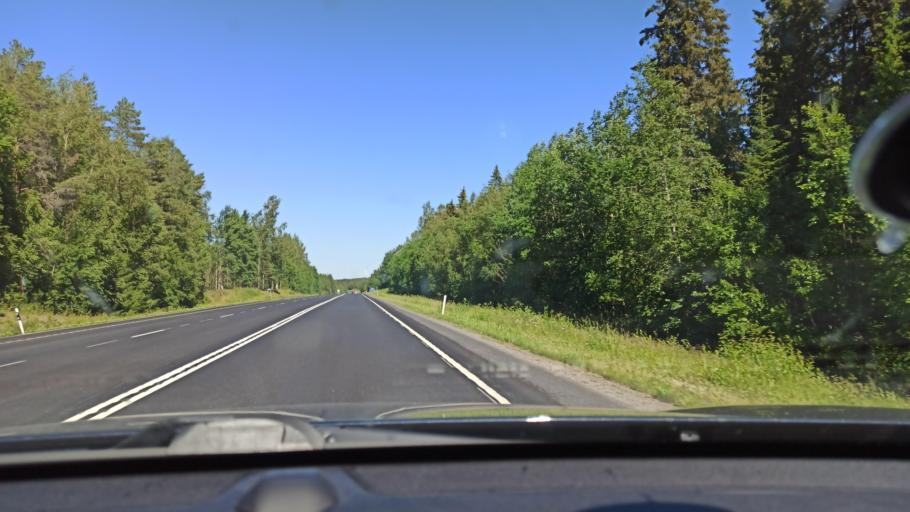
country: FI
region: Ostrobothnia
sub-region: Vaasa
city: Oravais
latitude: 63.2754
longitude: 22.3304
